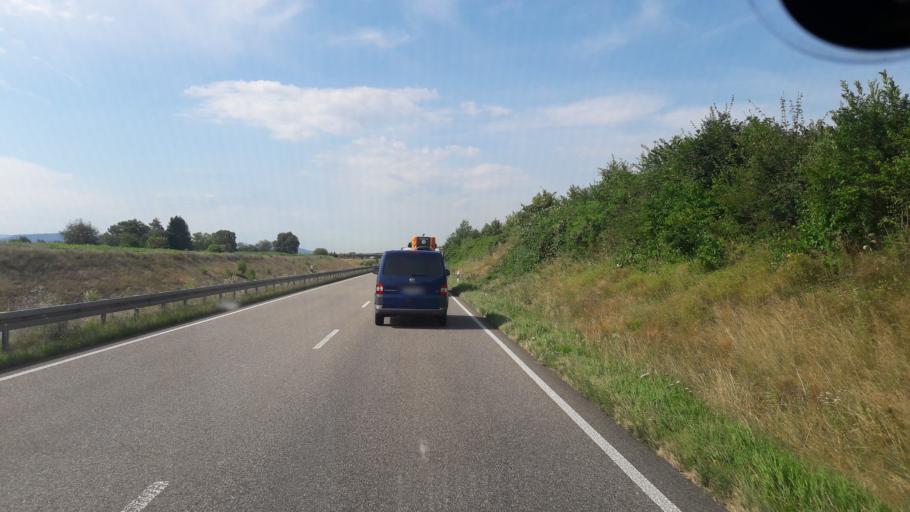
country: DE
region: Baden-Wuerttemberg
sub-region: Karlsruhe Region
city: Otigheim
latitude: 48.8916
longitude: 8.2519
